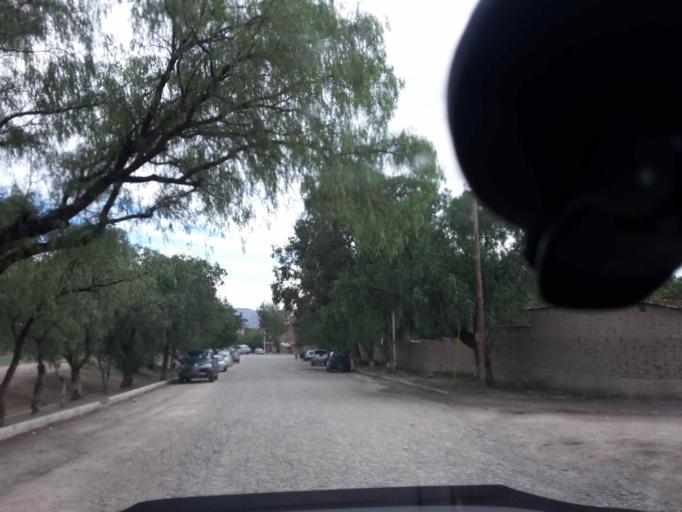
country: BO
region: Cochabamba
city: Cochabamba
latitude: -17.3369
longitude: -66.2133
